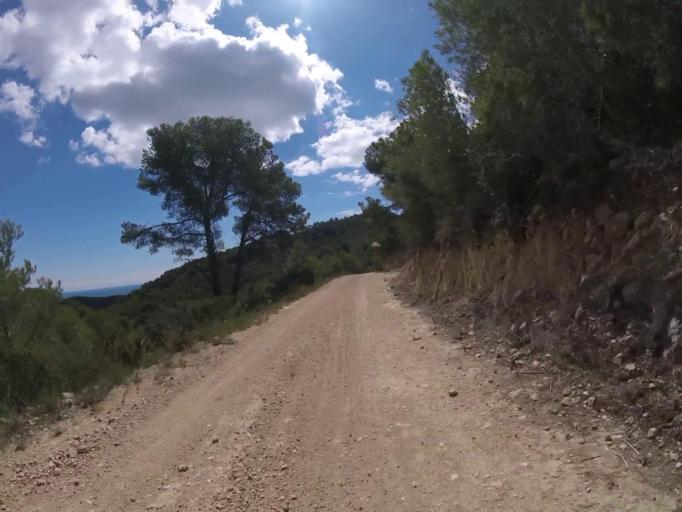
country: ES
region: Valencia
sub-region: Provincia de Castello
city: Santa Magdalena de Pulpis
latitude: 40.3102
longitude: 0.3196
